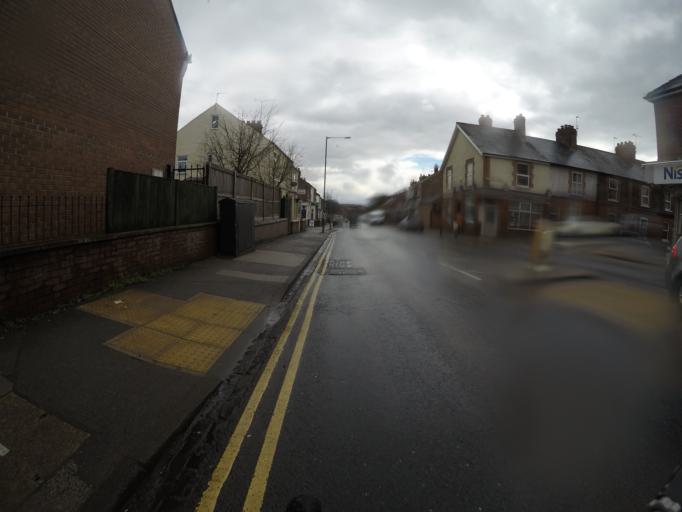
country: GB
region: England
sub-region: City of York
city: York
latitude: 53.9612
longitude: -1.1140
